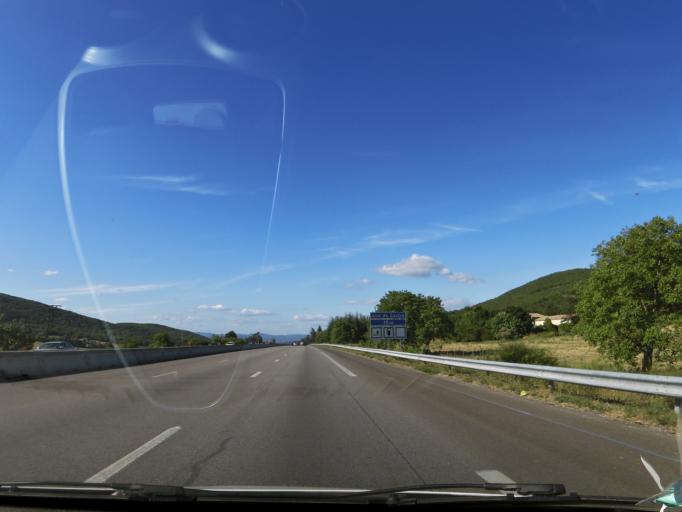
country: FR
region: Rhone-Alpes
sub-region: Departement de la Drome
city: Savasse
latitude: 44.6200
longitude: 4.7931
